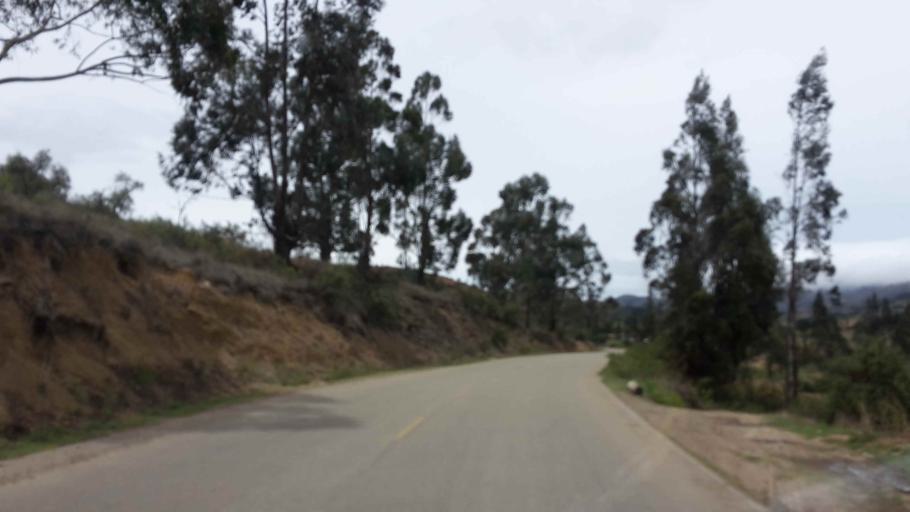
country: BO
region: Cochabamba
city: Totora
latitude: -17.7091
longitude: -65.2109
